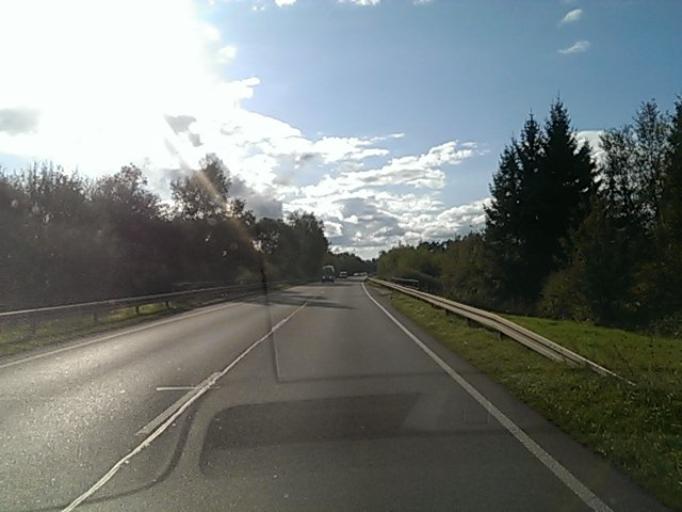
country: DE
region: Baden-Wuerttemberg
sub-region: Freiburg Region
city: Zimmern ob Rottweil
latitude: 48.1770
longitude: 8.5830
